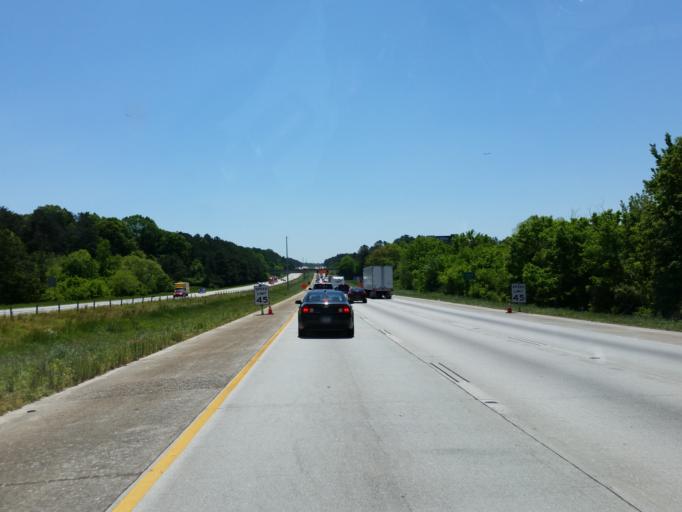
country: US
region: Georgia
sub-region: Clayton County
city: Conley
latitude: 33.6485
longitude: -84.3196
